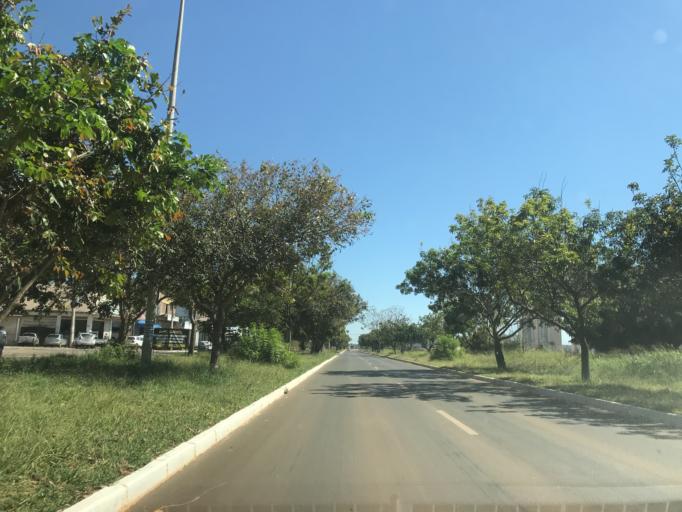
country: BR
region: Federal District
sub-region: Brasilia
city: Brasilia
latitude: -15.8029
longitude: -48.0917
